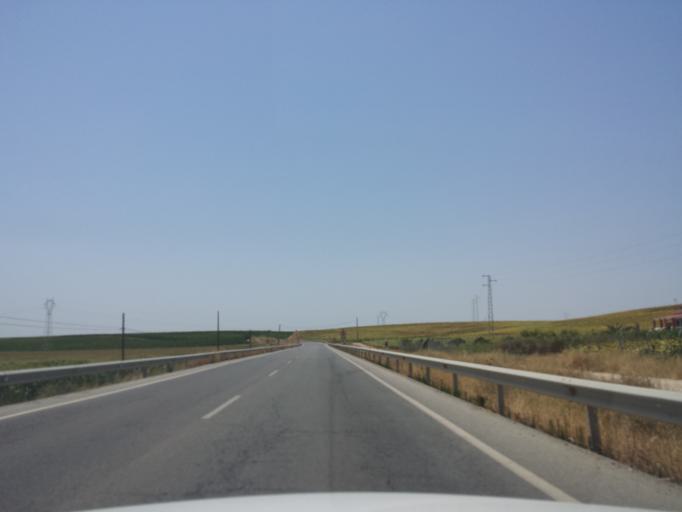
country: ES
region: Andalusia
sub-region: Provincia de Sevilla
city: Acala del Rio
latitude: 37.5351
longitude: -5.9574
